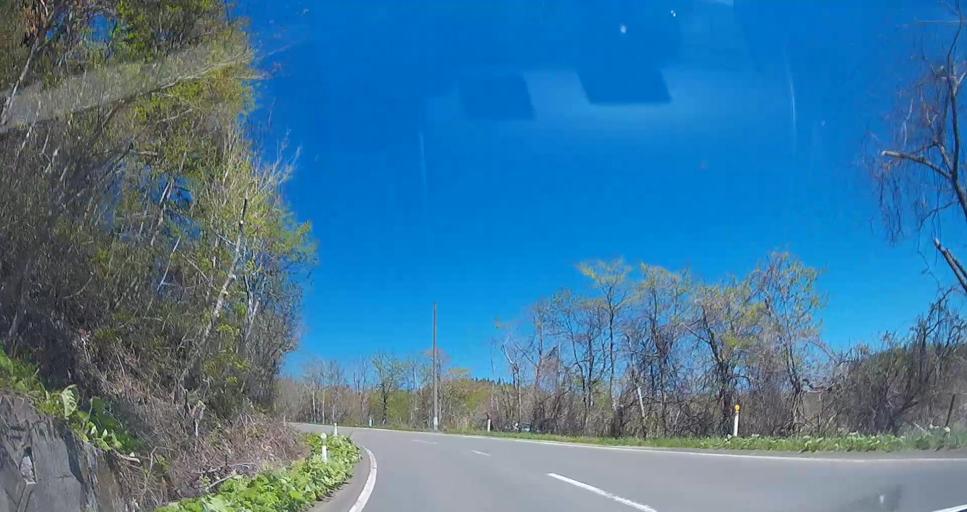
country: JP
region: Aomori
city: Mutsu
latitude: 41.2642
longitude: 141.3918
